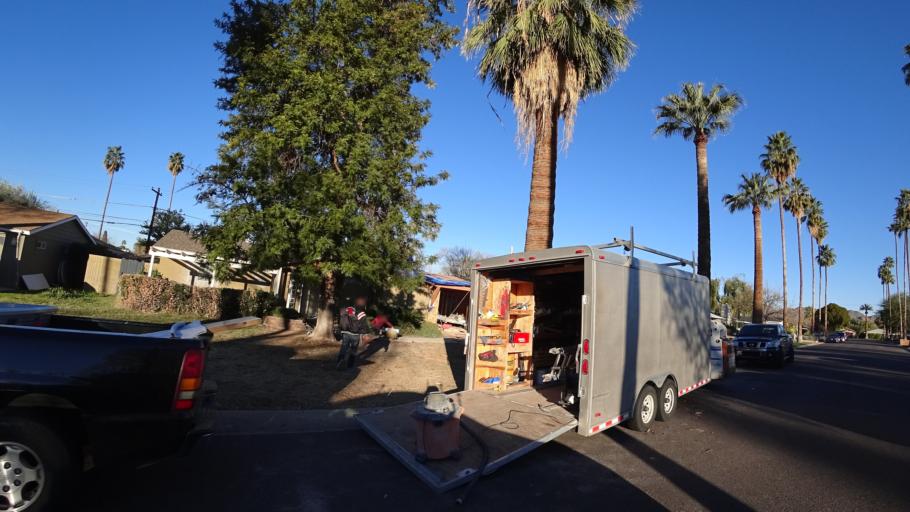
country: US
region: Arizona
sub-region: Maricopa County
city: Paradise Valley
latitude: 33.4972
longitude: -112.0077
